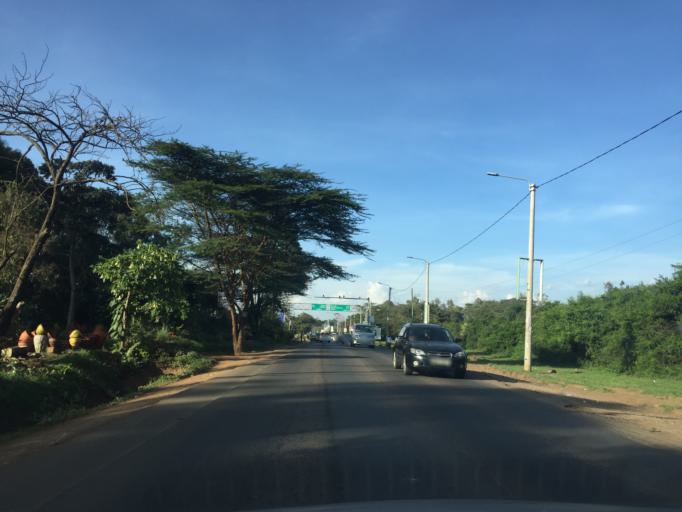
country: KE
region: Nairobi Area
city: Nairobi
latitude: -1.3477
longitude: 36.7650
